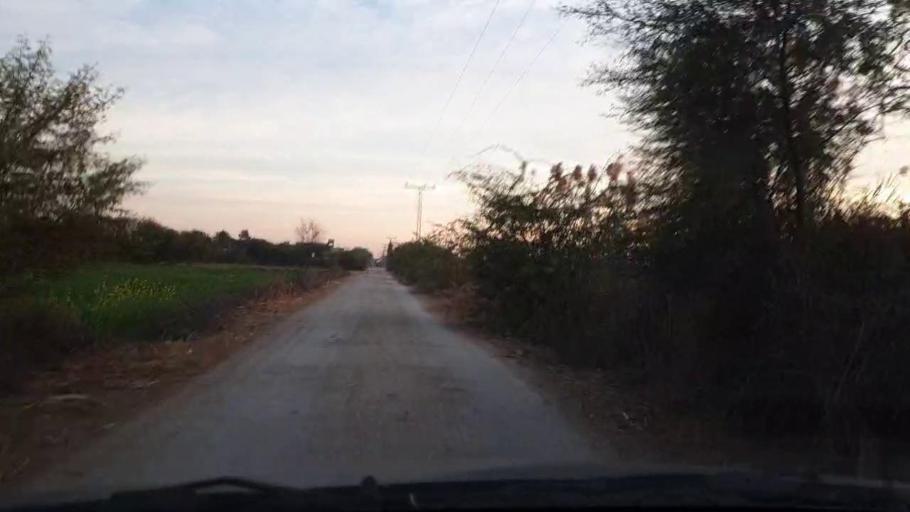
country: PK
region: Sindh
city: Sinjhoro
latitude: 26.1072
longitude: 68.7967
